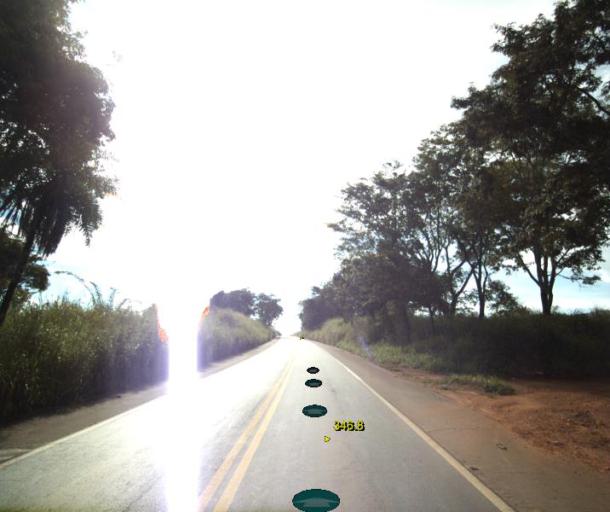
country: BR
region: Goias
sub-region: Jaragua
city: Jaragua
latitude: -15.6353
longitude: -49.3756
